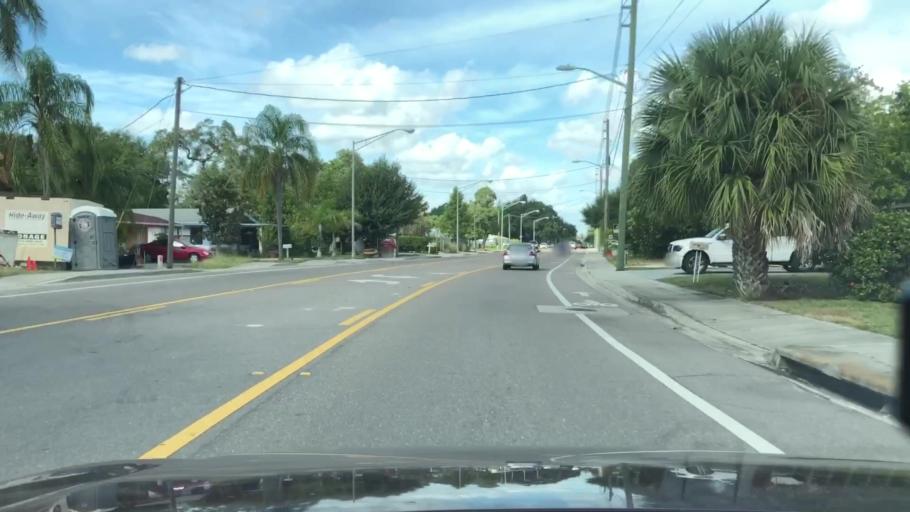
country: US
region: Florida
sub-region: Sarasota County
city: Sarasota Springs
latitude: 27.3031
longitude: -82.4822
